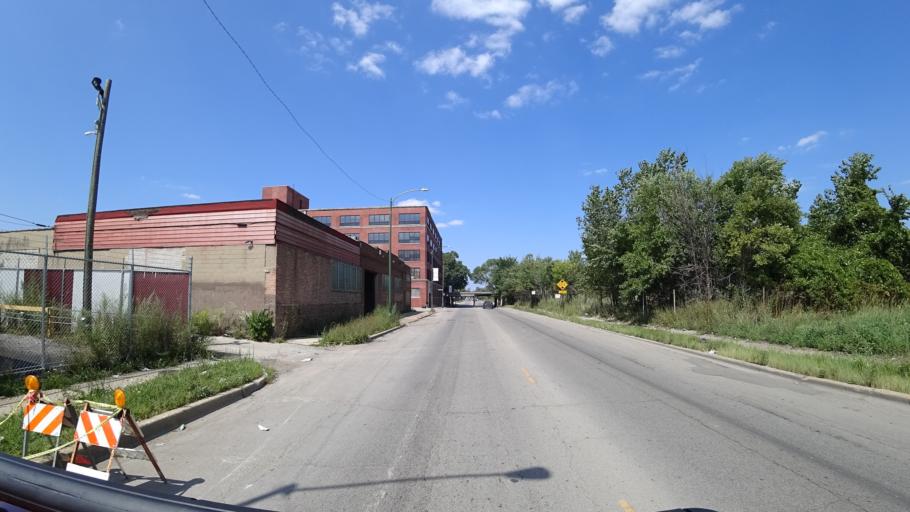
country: US
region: Illinois
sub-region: Cook County
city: Cicero
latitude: 41.8673
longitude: -87.7350
